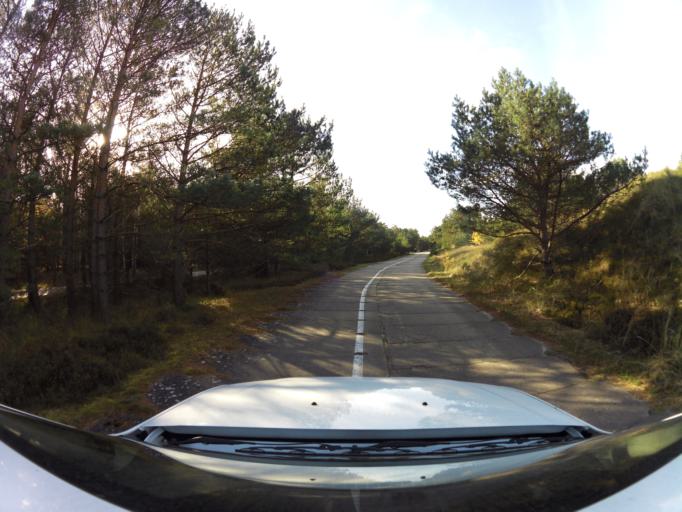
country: PL
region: West Pomeranian Voivodeship
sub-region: Powiat gryficki
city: Cerkwica
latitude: 54.1117
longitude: 15.1528
